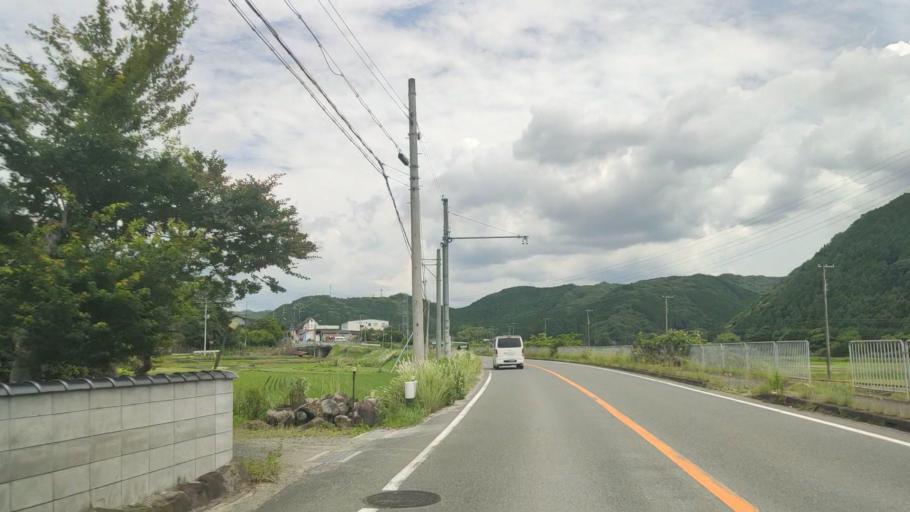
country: JP
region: Hyogo
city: Yamazakicho-nakabirose
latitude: 34.9822
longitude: 134.4177
